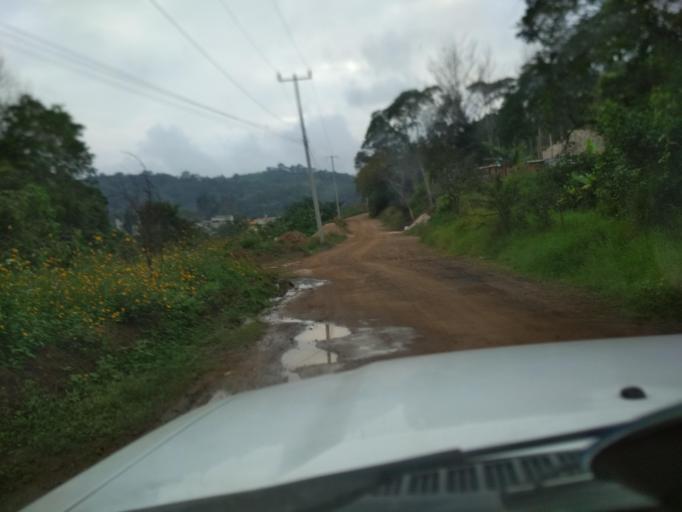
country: MX
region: Veracruz
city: El Castillo
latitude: 19.5638
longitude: -96.8568
